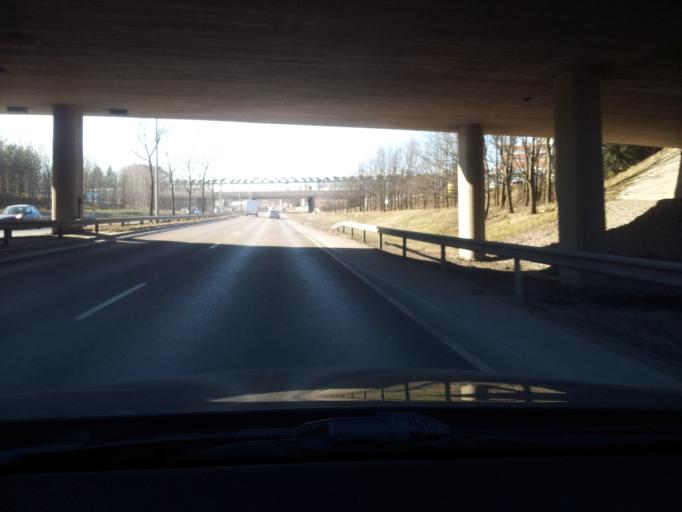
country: FI
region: Uusimaa
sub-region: Helsinki
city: Vantaa
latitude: 60.2417
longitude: 24.9972
